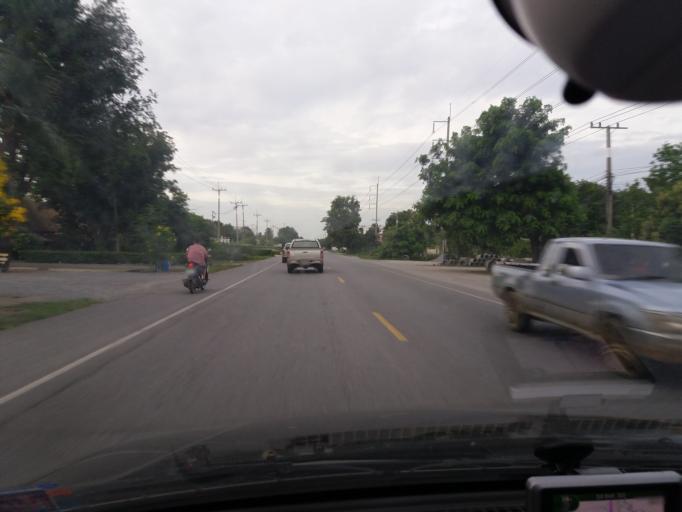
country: TH
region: Suphan Buri
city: U Thong
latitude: 14.5019
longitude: 99.9186
